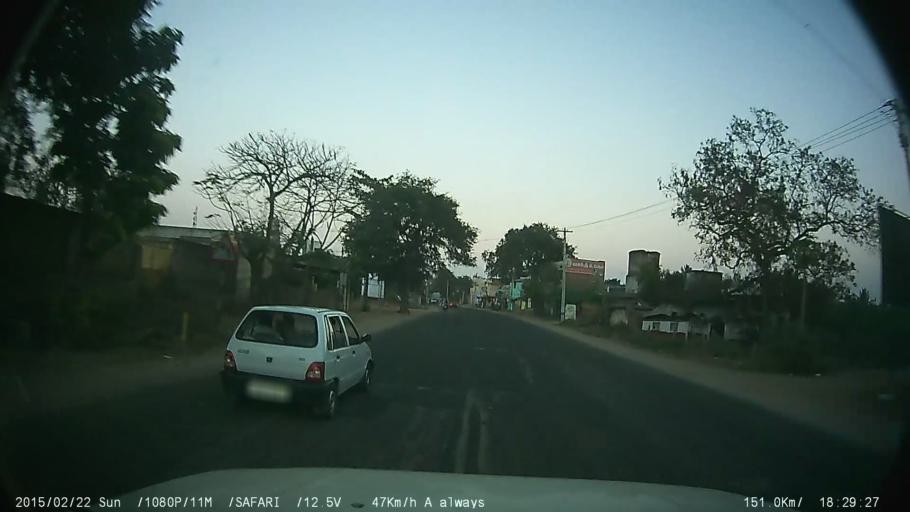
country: IN
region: Tamil Nadu
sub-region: Theni
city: Teni
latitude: 9.9845
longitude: 77.4544
